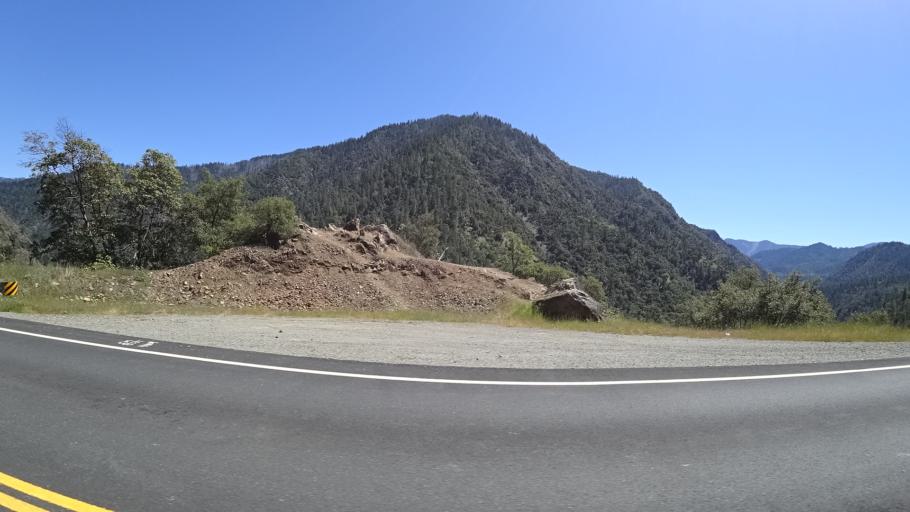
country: US
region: California
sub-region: Humboldt County
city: Willow Creek
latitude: 40.8449
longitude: -123.4837
